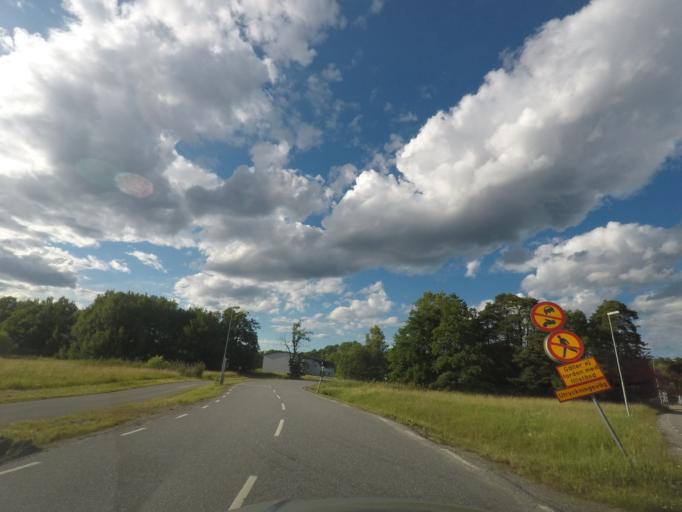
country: SE
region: Stockholm
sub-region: Sigtuna Kommun
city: Marsta
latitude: 59.6378
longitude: 17.9034
